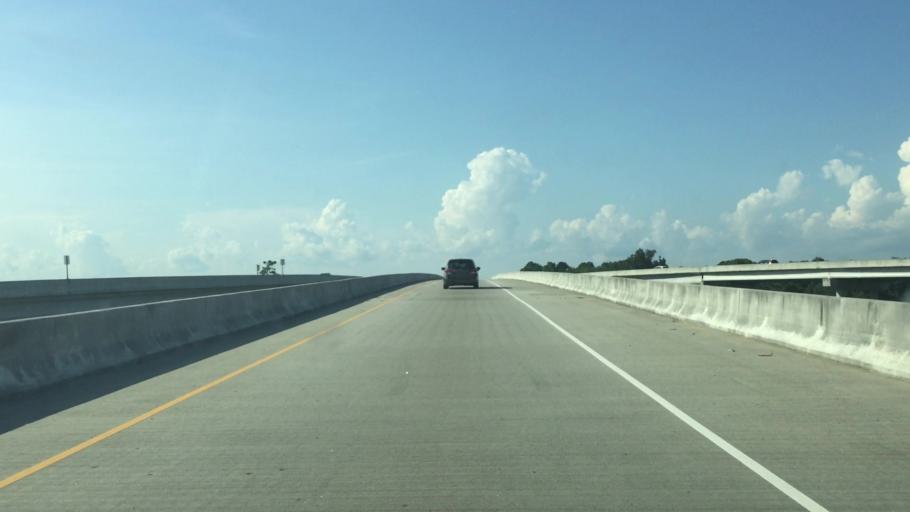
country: US
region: South Carolina
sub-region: Horry County
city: North Myrtle Beach
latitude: 33.7882
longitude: -78.7763
